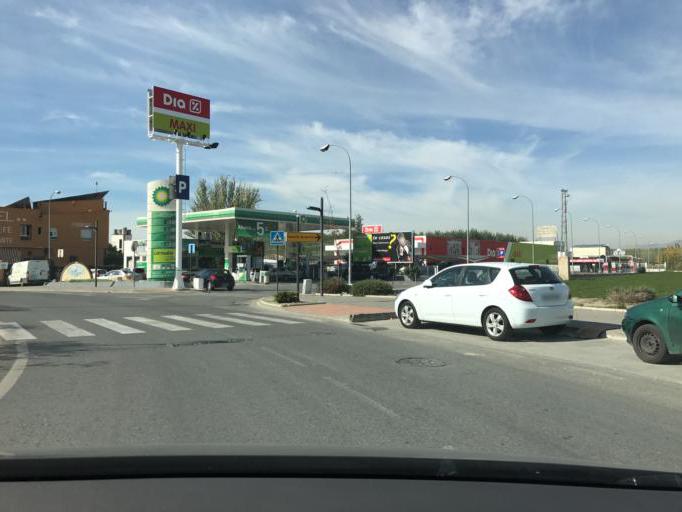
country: ES
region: Andalusia
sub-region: Provincia de Granada
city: Atarfe
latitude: 37.1926
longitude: -3.7087
